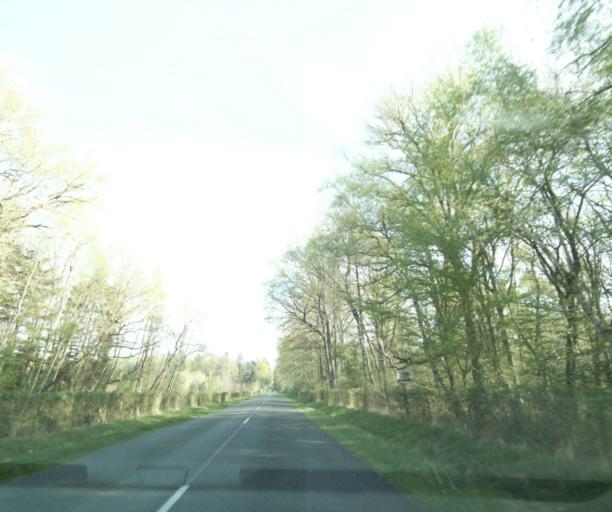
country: FR
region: Ile-de-France
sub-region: Departement de Seine-et-Marne
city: Vernou-la-Celle-sur-Seine
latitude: 48.4320
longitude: 2.8496
